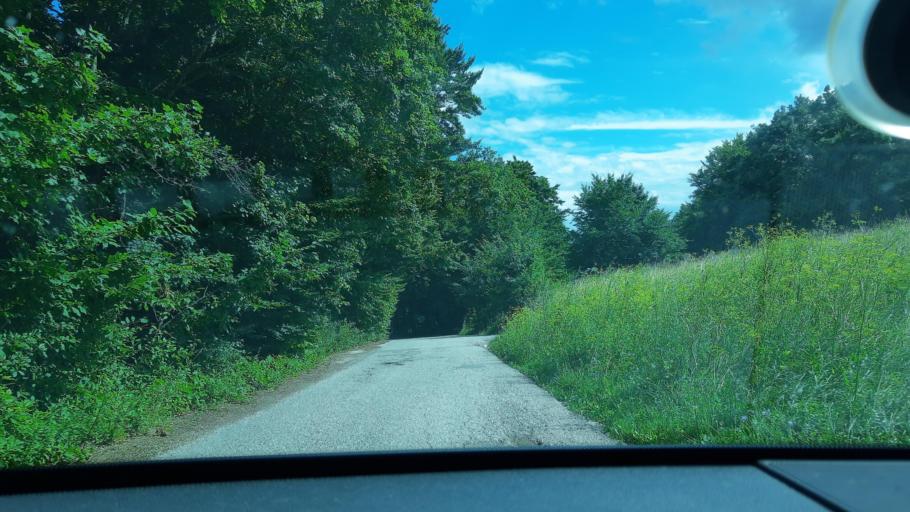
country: SK
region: Trnavsky
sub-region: Okres Trnava
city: Piestany
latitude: 48.6617
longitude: 17.9666
